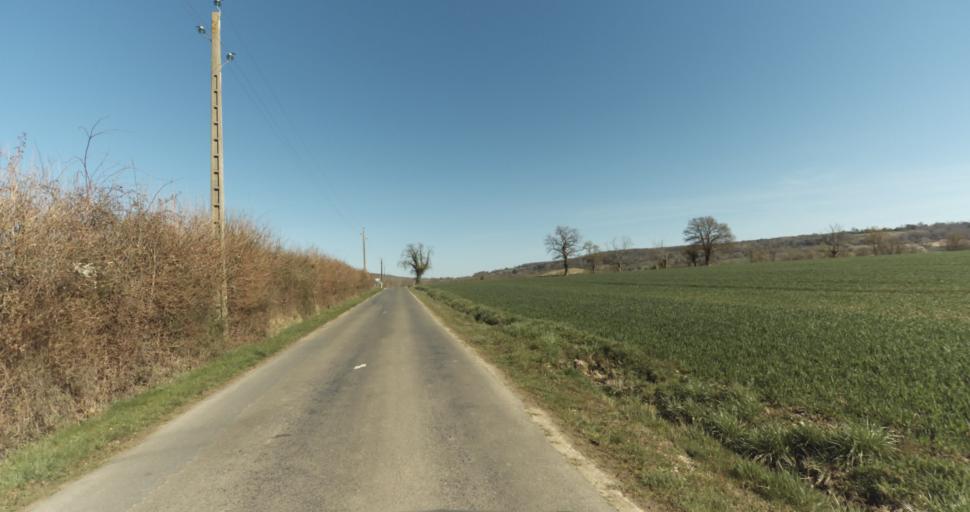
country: FR
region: Lower Normandy
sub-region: Departement du Calvados
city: Saint-Pierre-sur-Dives
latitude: 48.9577
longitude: 0.0500
